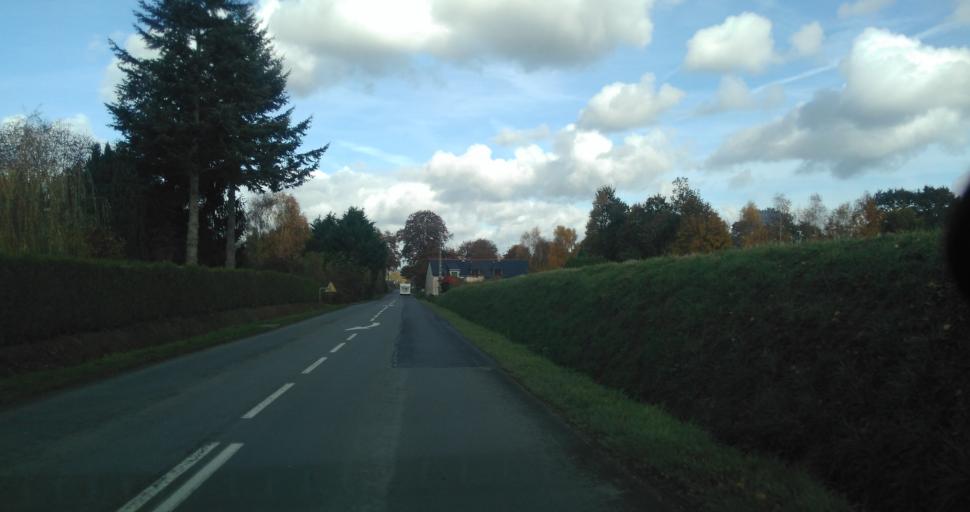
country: FR
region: Brittany
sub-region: Departement d'Ille-et-Vilaine
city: Boisgervilly
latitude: 48.1686
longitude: -2.0539
